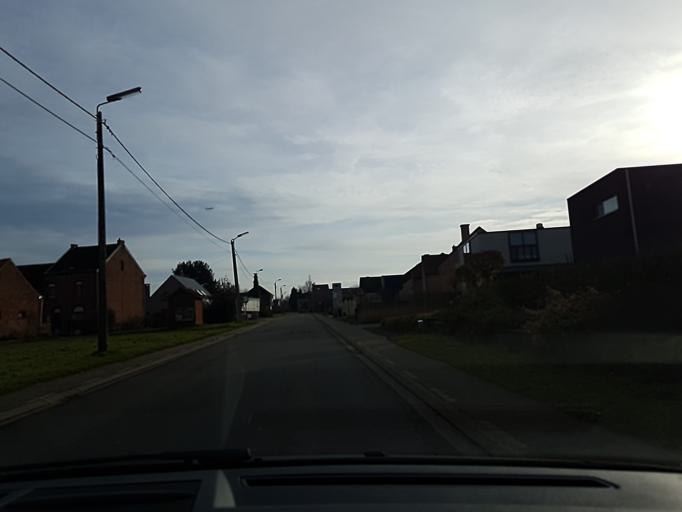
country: BE
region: Flanders
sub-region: Provincie Vlaams-Brabant
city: Haacht
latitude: 50.9619
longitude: 4.6646
